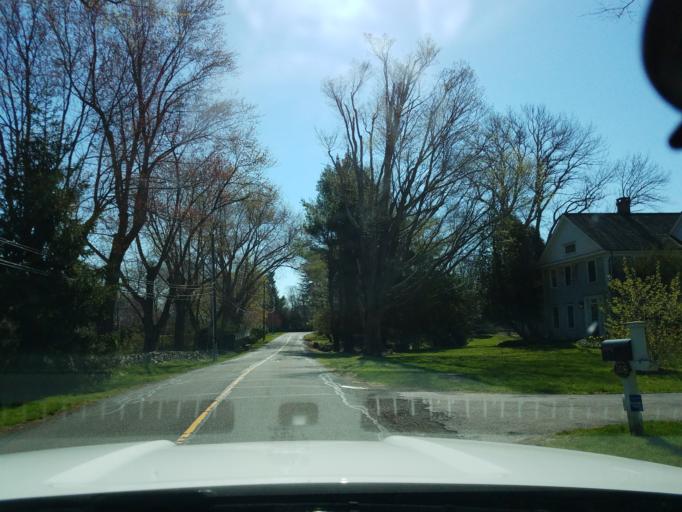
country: US
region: Connecticut
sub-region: Fairfield County
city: Southport
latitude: 41.1314
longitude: -73.3062
